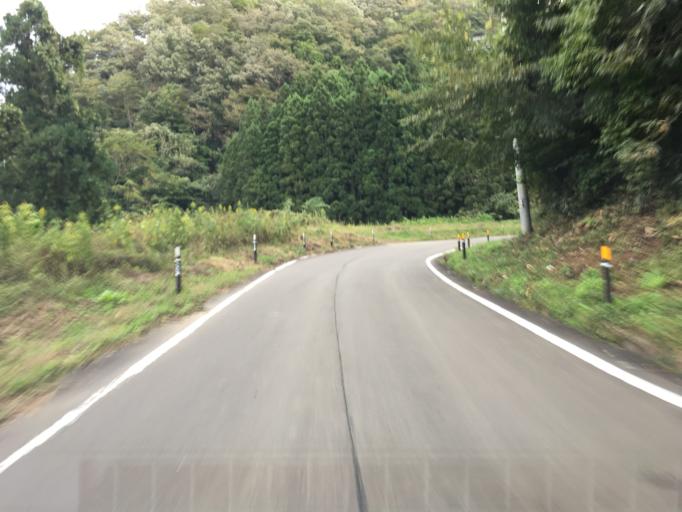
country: JP
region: Miyagi
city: Marumori
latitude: 37.9251
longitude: 140.7394
